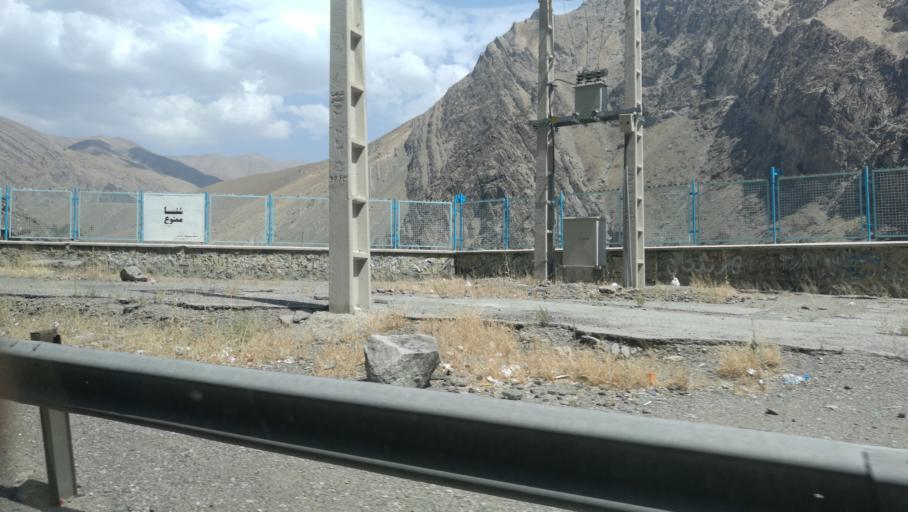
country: IR
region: Alborz
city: Karaj
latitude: 35.9603
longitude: 51.0901
